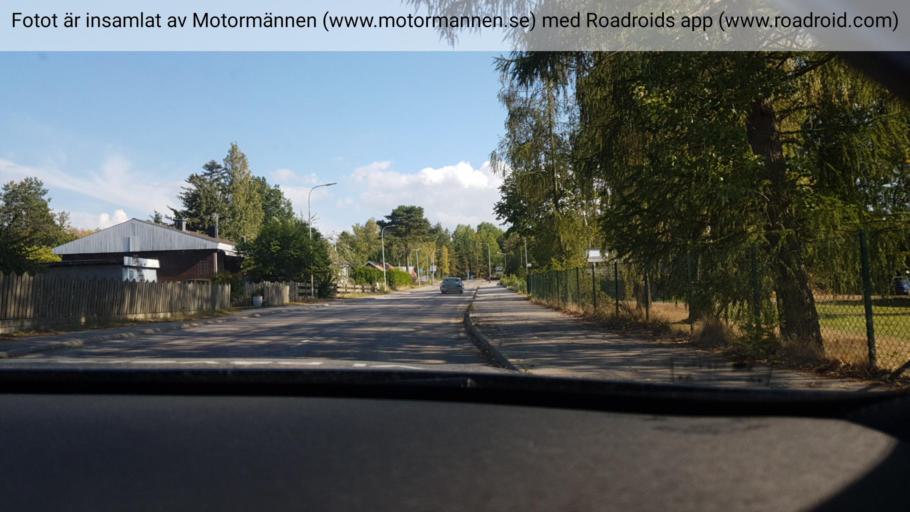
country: SE
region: Vaestra Goetaland
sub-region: Mariestads Kommun
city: Mariestad
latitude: 58.6430
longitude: 13.7001
